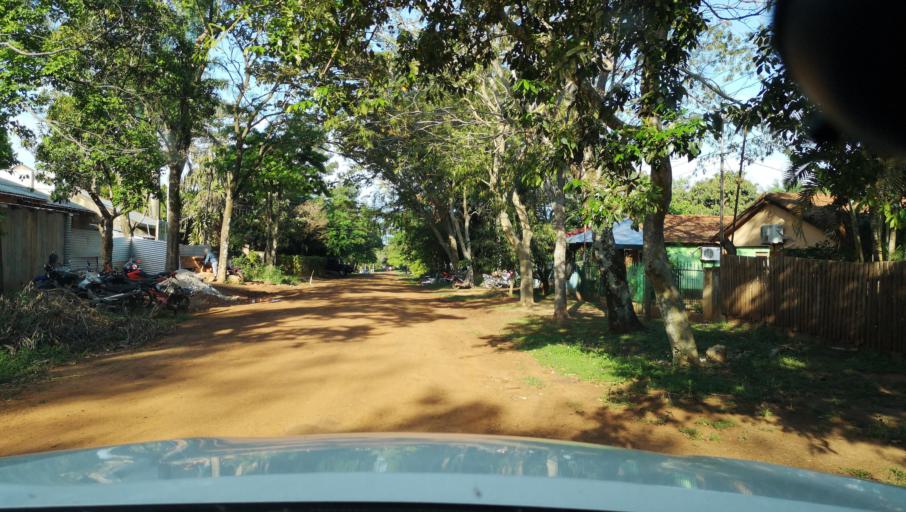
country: PY
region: Itapua
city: Carmen del Parana
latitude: -27.1608
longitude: -56.2471
